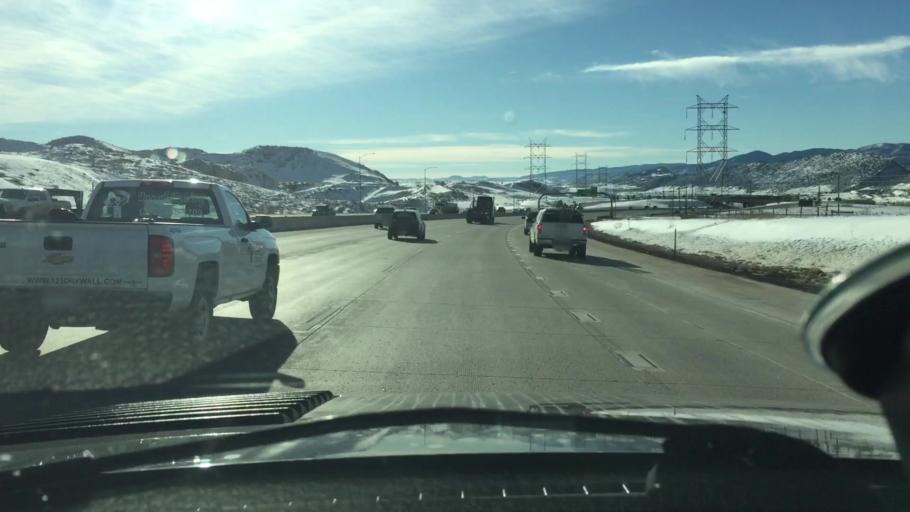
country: US
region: Colorado
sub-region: Jefferson County
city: West Pleasant View
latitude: 39.6935
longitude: -105.1891
